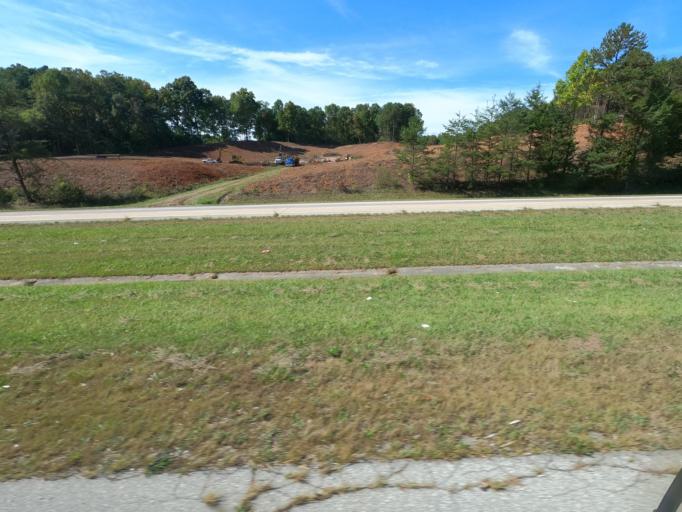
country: US
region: Tennessee
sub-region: Hamblen County
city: Morristown
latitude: 36.2358
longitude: -83.2616
